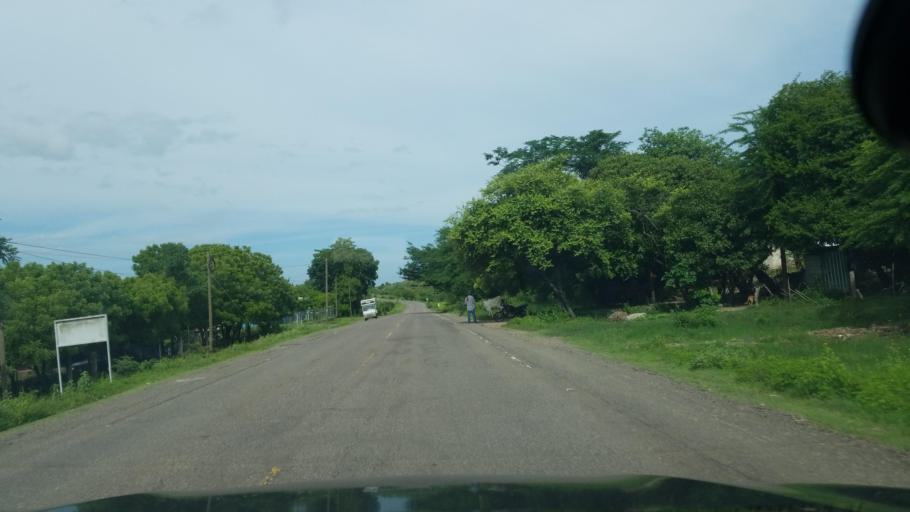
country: HN
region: Choluteca
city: Santa Ana de Yusguare
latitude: 13.3584
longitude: -87.0962
